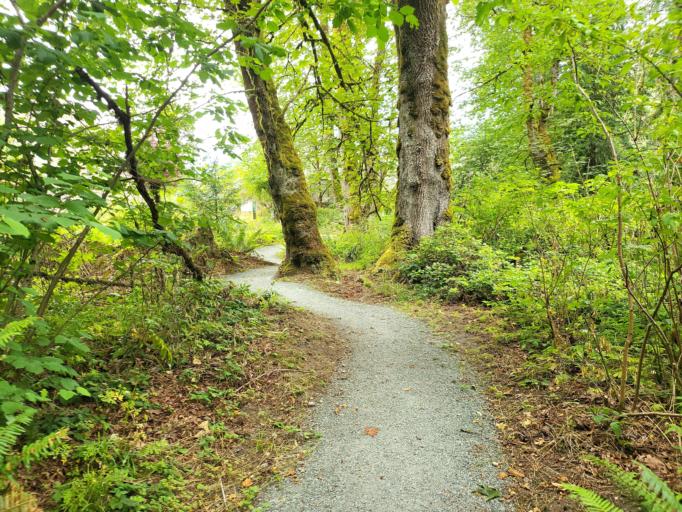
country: US
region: Washington
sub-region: King County
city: Newcastle
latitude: 47.5403
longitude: -122.1250
